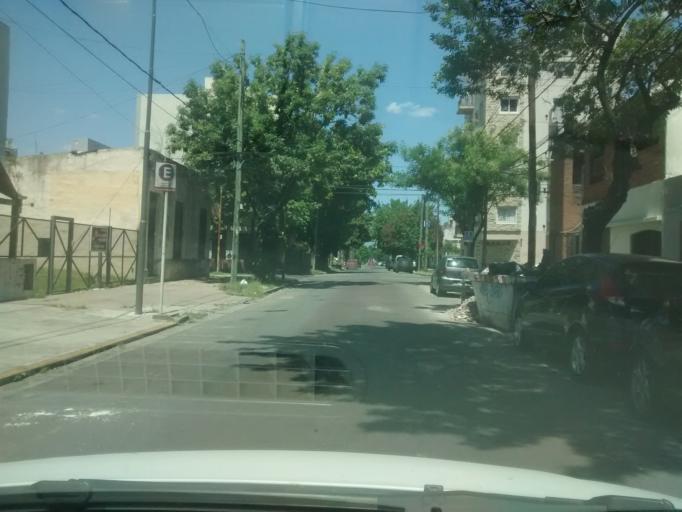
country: AR
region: Buenos Aires
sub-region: Partido de Moron
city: Moron
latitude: -34.6545
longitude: -58.6164
